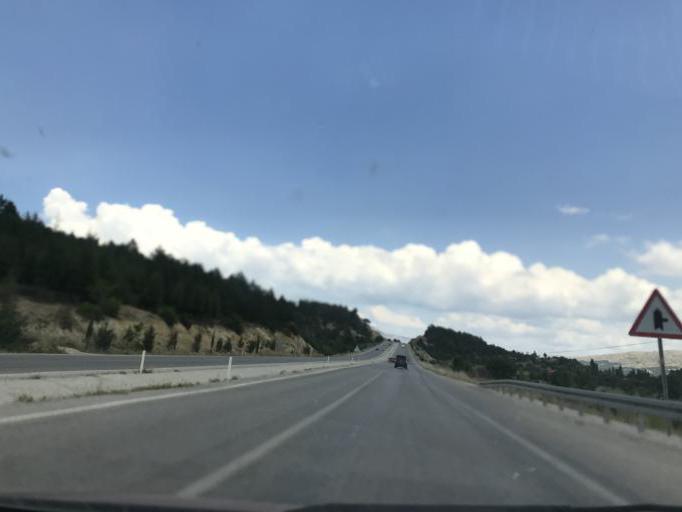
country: TR
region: Denizli
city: Tavas
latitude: 37.6134
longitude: 29.1564
